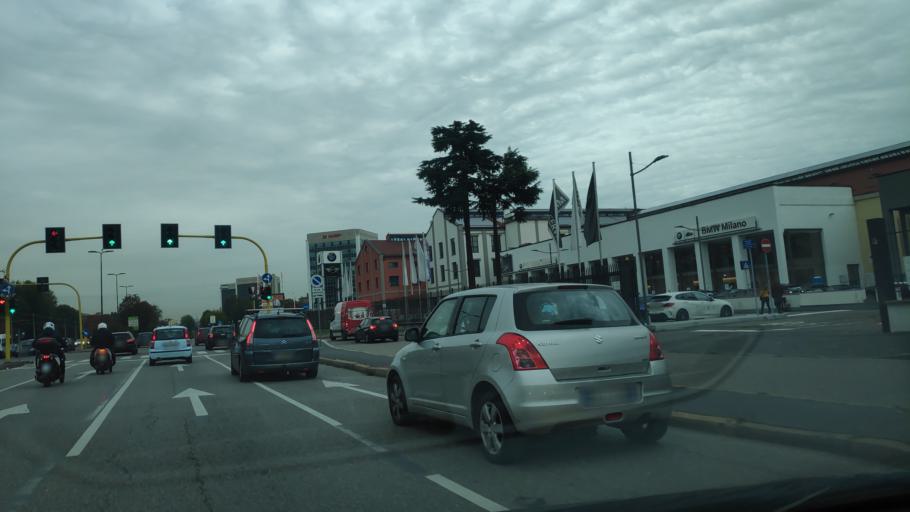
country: IT
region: Lombardy
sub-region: Citta metropolitana di Milano
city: Rozzano
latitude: 45.4138
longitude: 9.1751
